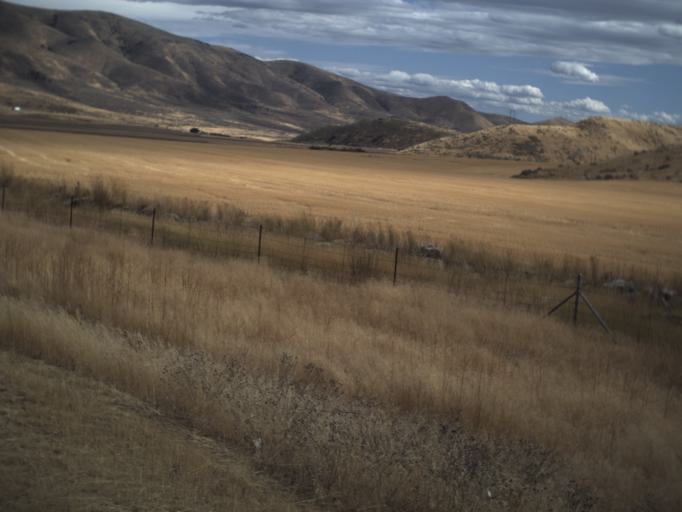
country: US
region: Utah
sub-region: Box Elder County
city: Garland
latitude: 41.7986
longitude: -112.3031
